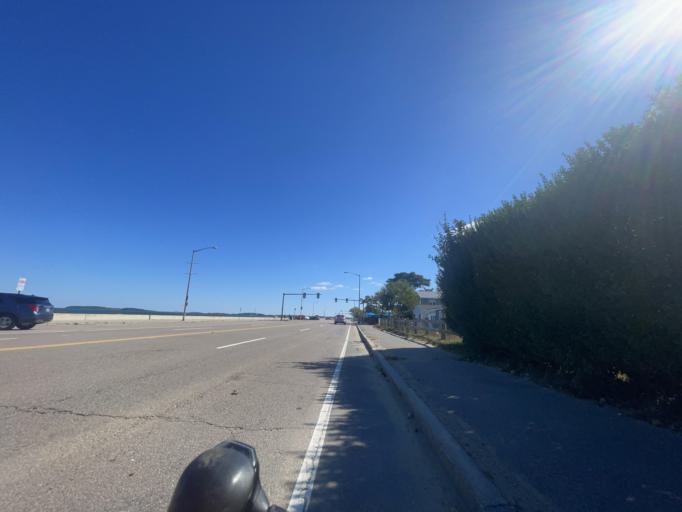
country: US
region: Massachusetts
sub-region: Norfolk County
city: Quincy
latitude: 42.2757
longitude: -71.0068
